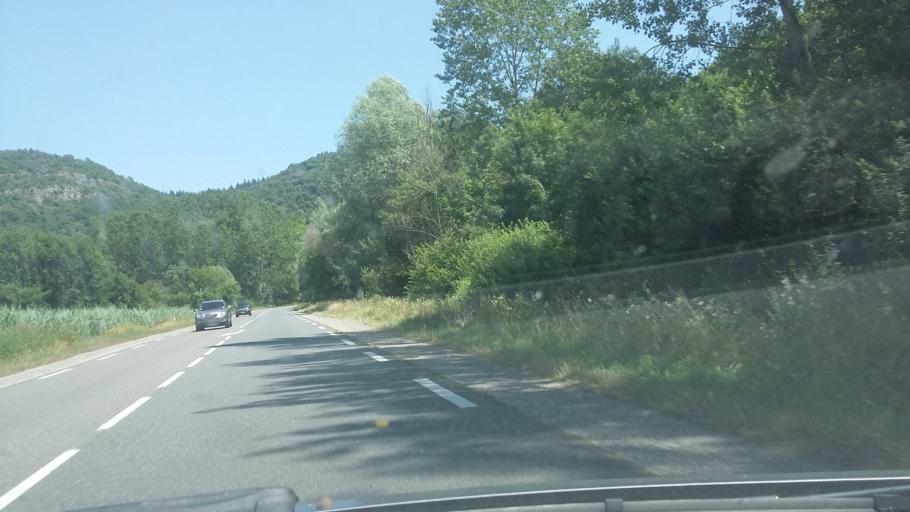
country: FR
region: Rhone-Alpes
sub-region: Departement de l'Ain
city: Belley
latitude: 45.7786
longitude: 5.7041
